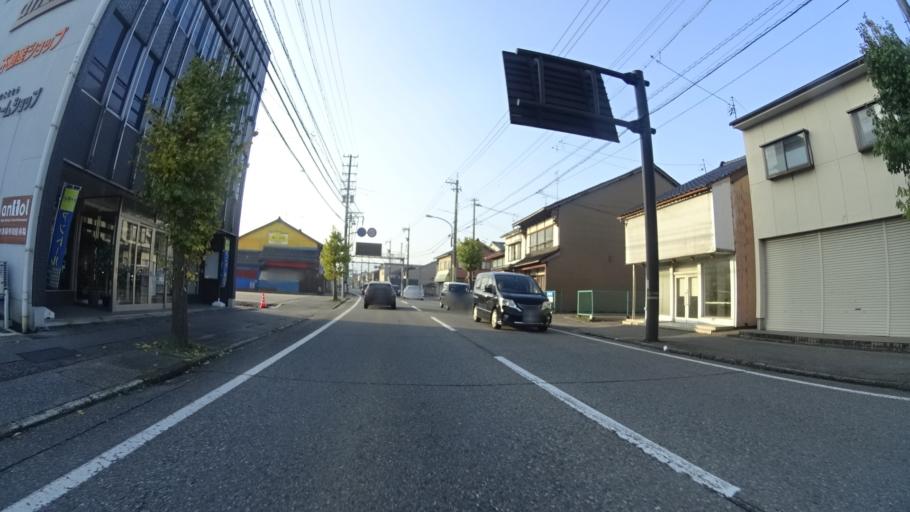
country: JP
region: Ishikawa
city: Nanao
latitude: 37.0412
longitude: 136.9696
